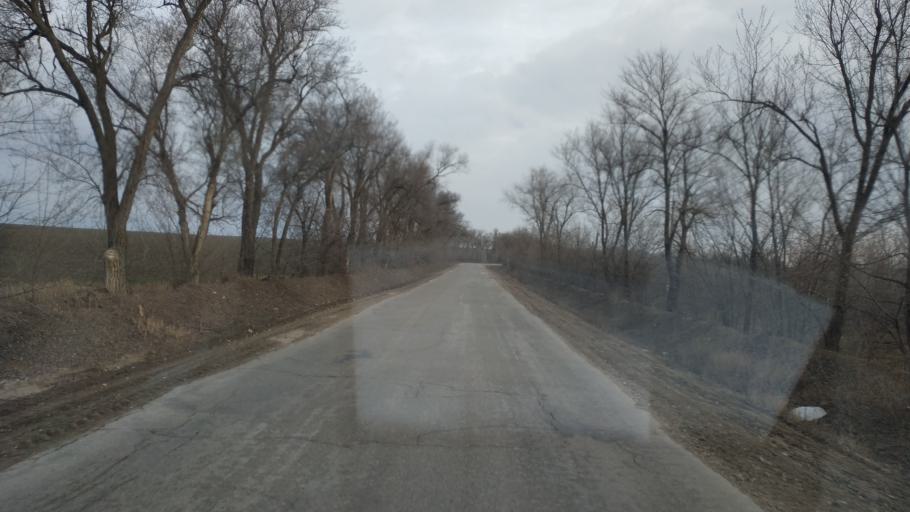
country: MD
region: Chisinau
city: Singera
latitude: 46.9403
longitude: 29.0486
